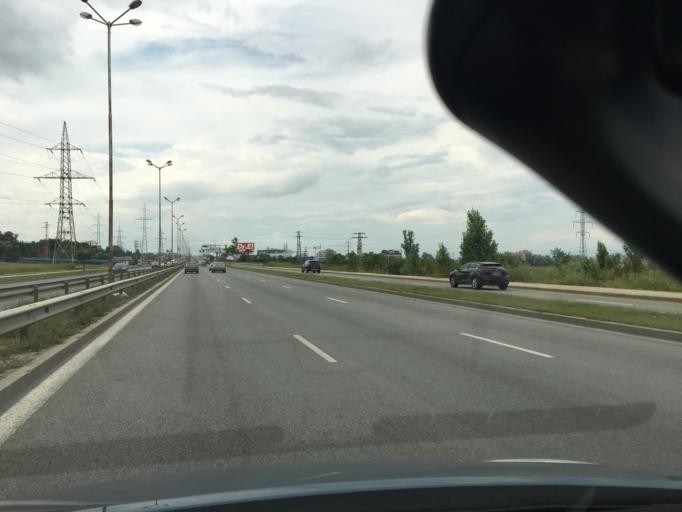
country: BG
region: Sofia-Capital
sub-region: Stolichna Obshtina
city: Sofia
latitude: 42.6293
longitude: 23.3428
